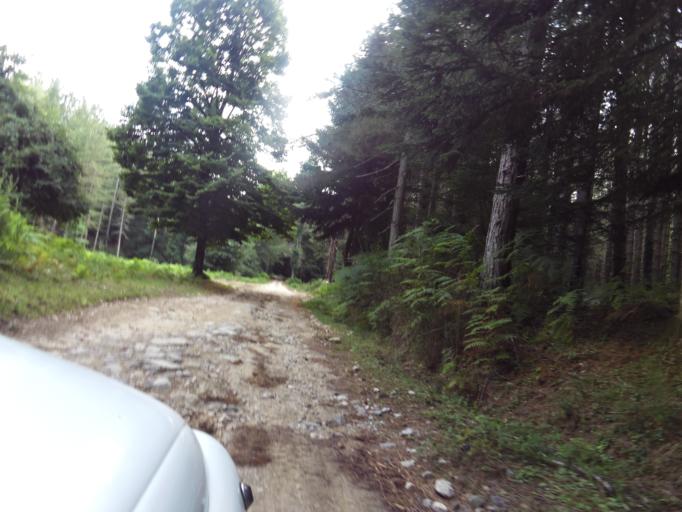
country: IT
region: Calabria
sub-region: Provincia di Vibo-Valentia
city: Nardodipace
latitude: 38.5147
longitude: 16.3789
